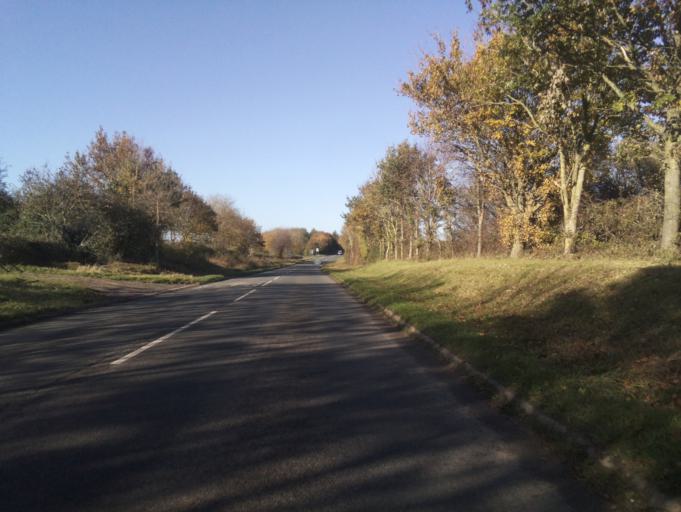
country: GB
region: England
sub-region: Somerset
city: Stoke-sub-Hamdon
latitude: 50.9732
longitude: -2.7231
